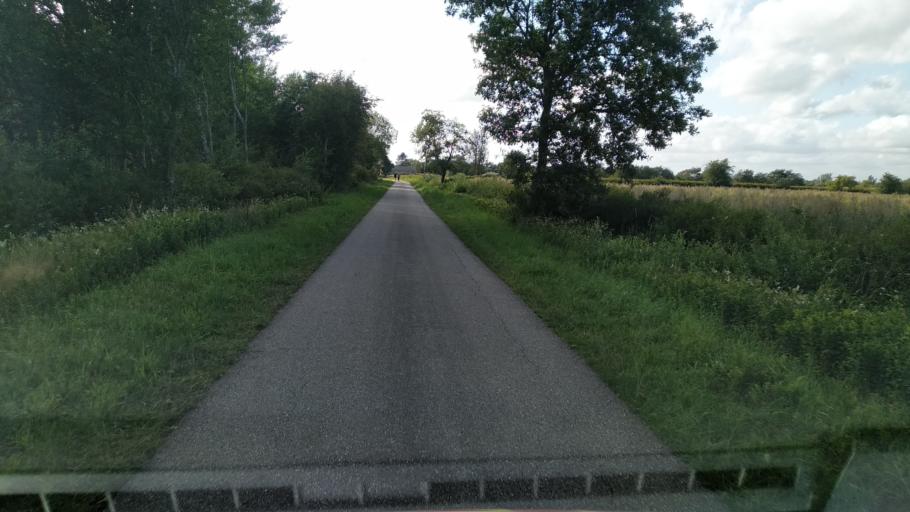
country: DE
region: Schleswig-Holstein
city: Gross Rheide
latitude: 54.4276
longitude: 9.4268
